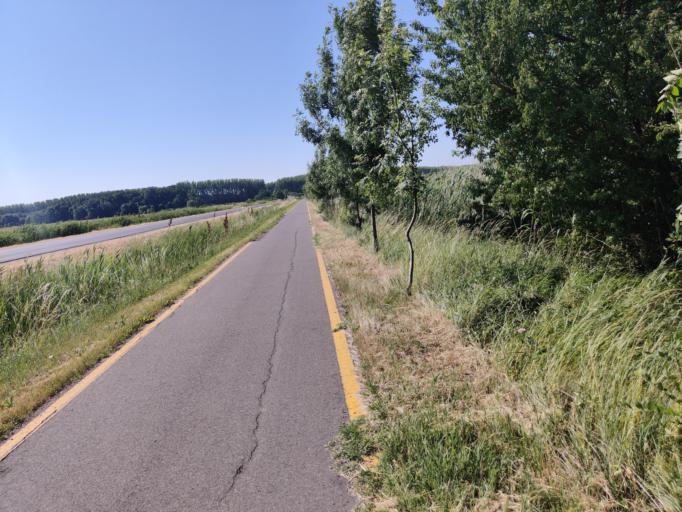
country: HU
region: Hajdu-Bihar
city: Balmazujvaros
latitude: 47.5887
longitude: 21.3441
